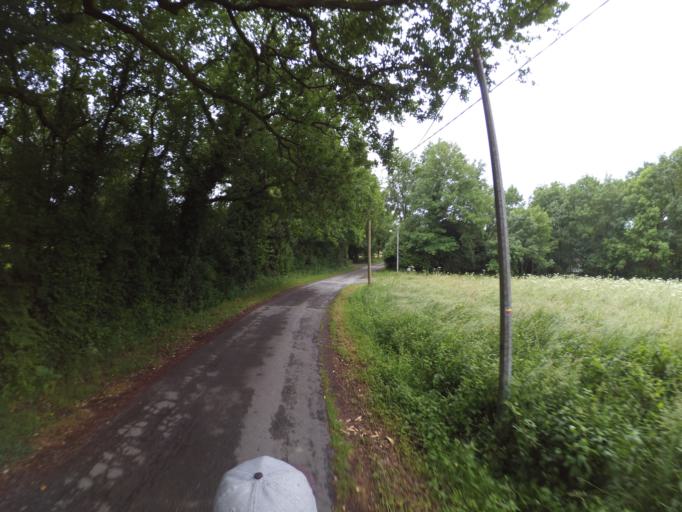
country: FR
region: Pays de la Loire
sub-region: Departement de la Vendee
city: La Roche-sur-Yon
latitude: 46.6298
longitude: -1.4248
